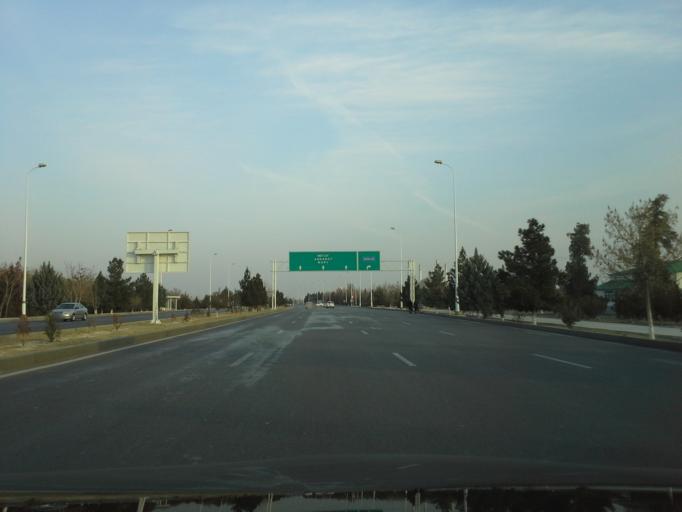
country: TM
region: Ahal
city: Abadan
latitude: 38.0260
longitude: 58.2399
